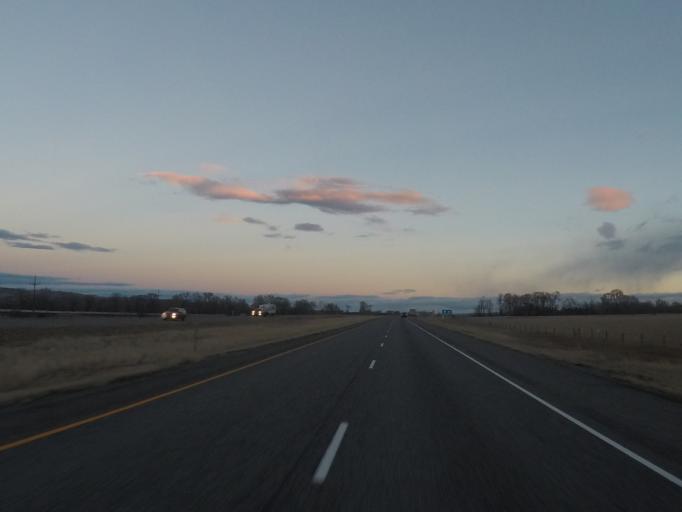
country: US
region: Montana
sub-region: Sweet Grass County
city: Big Timber
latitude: 45.7816
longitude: -109.8088
